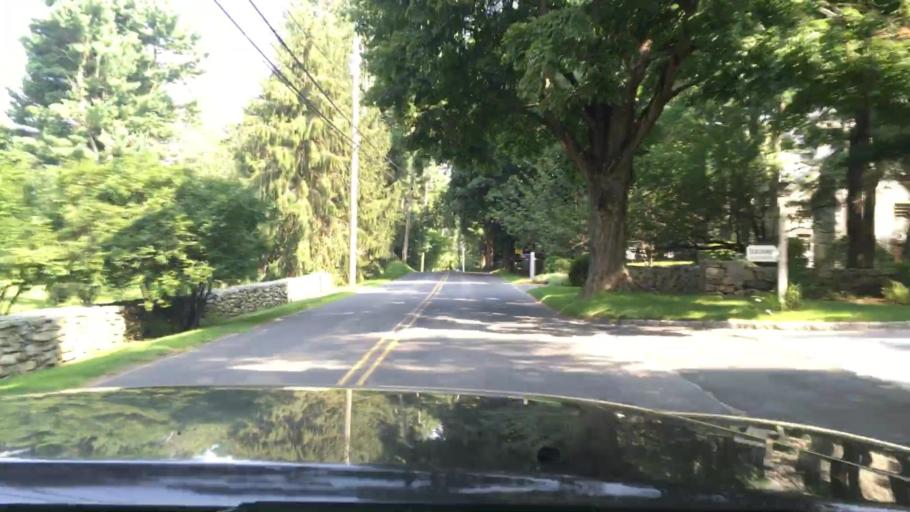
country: US
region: Connecticut
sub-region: Fairfield County
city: Georgetown
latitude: 41.2325
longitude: -73.4602
